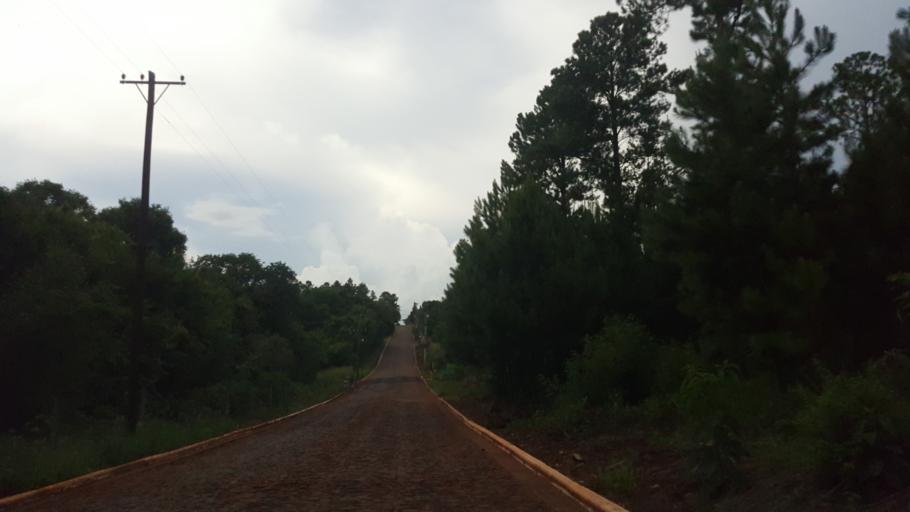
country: AR
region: Misiones
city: Jardin America
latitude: -27.0801
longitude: -55.2864
